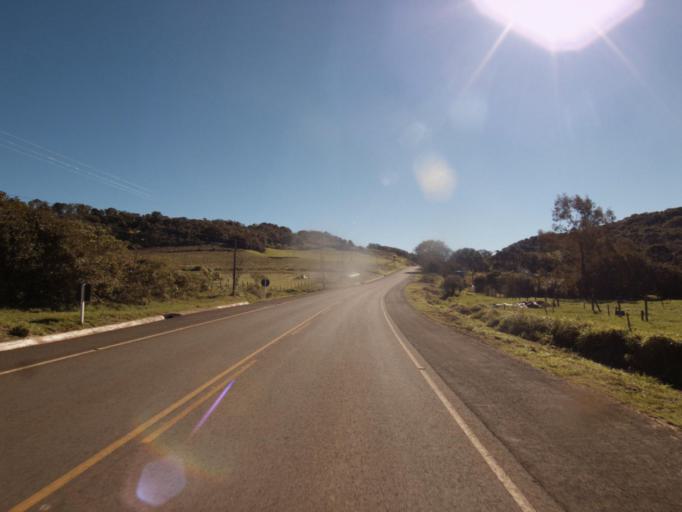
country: AR
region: Misiones
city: Bernardo de Irigoyen
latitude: -26.6467
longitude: -53.6207
